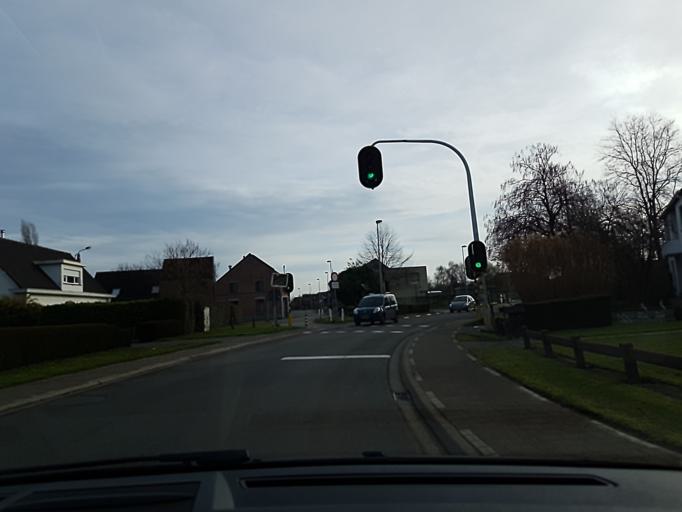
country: BE
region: Flanders
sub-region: Provincie Vlaams-Brabant
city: Haacht
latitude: 50.9587
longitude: 4.6725
